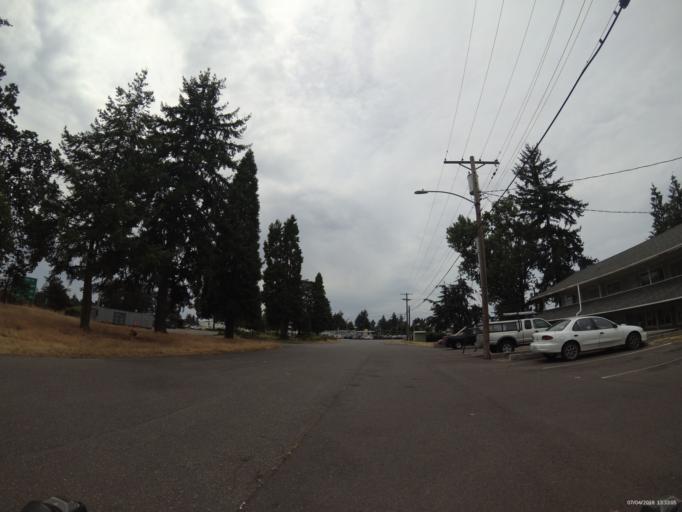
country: US
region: Washington
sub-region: Pierce County
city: McChord Air Force Base
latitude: 47.1559
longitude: -122.4907
